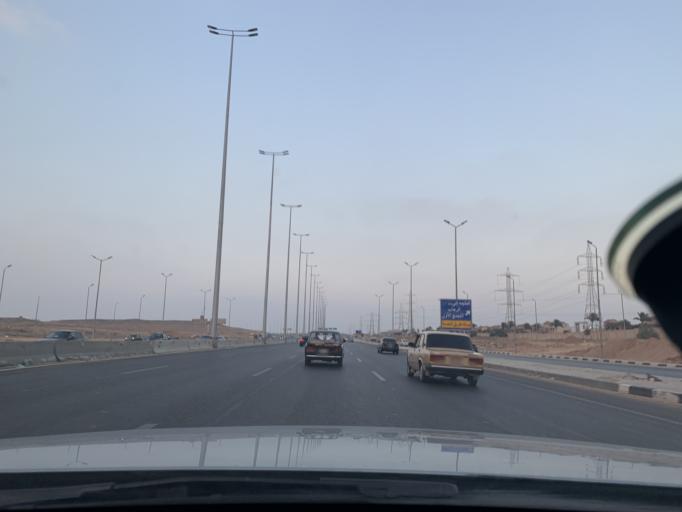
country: EG
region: Muhafazat al Qalyubiyah
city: Al Khankah
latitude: 30.0797
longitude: 31.4373
